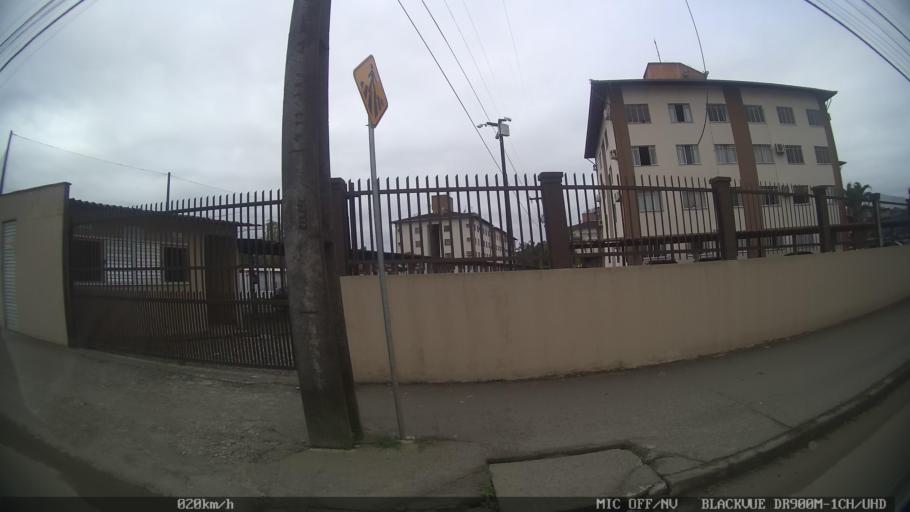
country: BR
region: Santa Catarina
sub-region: Joinville
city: Joinville
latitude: -26.2683
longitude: -48.8909
